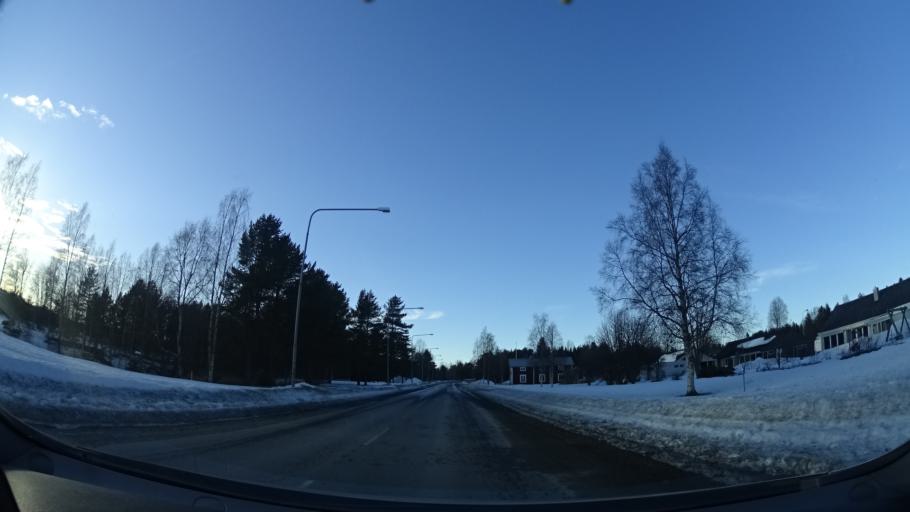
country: SE
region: Vaesterbotten
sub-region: Skelleftea Kommun
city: Byske
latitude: 64.9484
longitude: 21.2245
